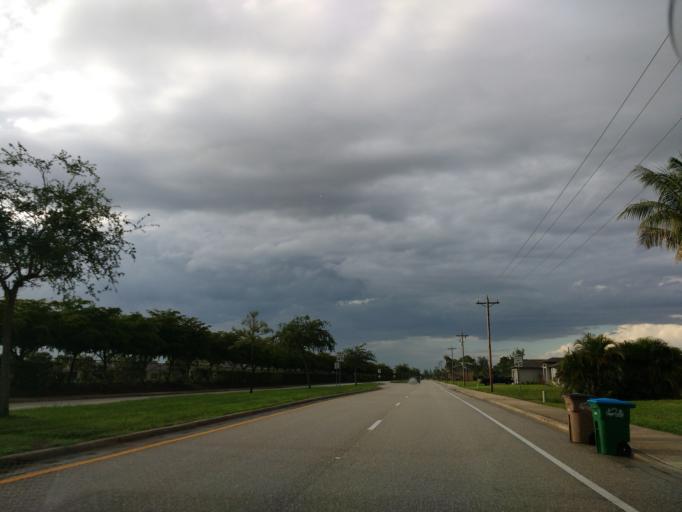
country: US
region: Florida
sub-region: Lee County
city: Cape Coral
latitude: 26.6133
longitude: -82.0233
